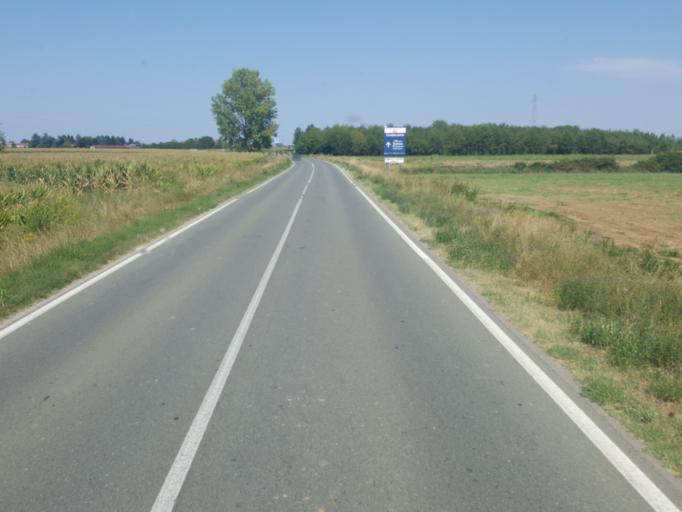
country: IT
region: Piedmont
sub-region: Provincia di Alessandria
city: Castelceriolo
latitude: 44.9044
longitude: 8.6861
